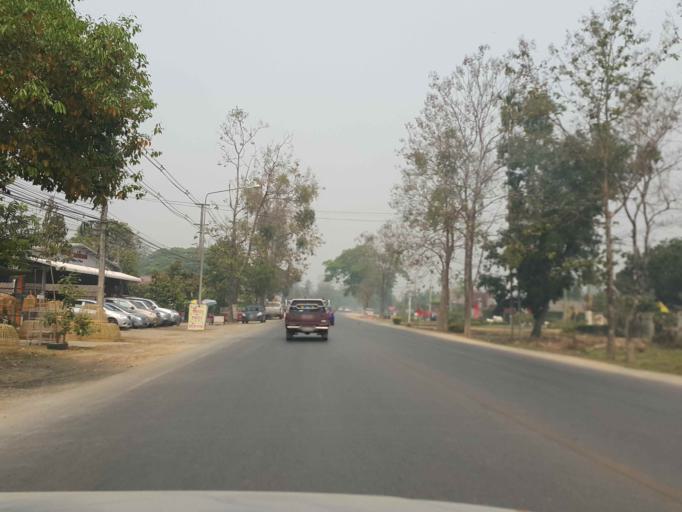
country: TH
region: Chiang Mai
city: San Sai
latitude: 18.9276
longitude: 98.9912
